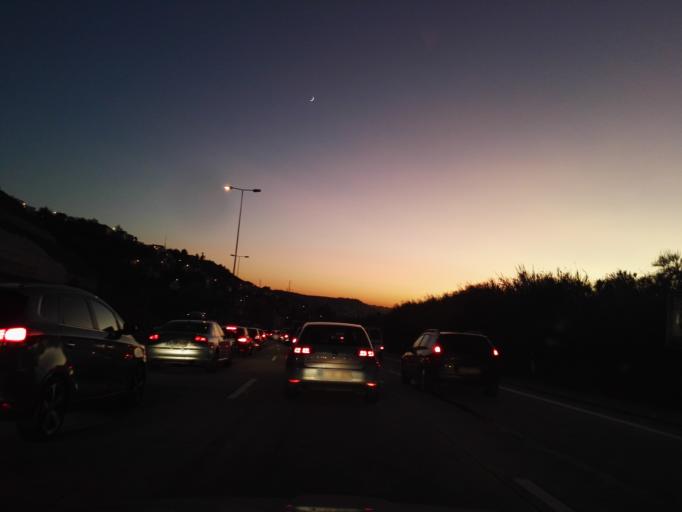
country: PT
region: Lisbon
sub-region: Odivelas
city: Povoa de Santo Adriao
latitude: 38.7994
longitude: -9.1525
